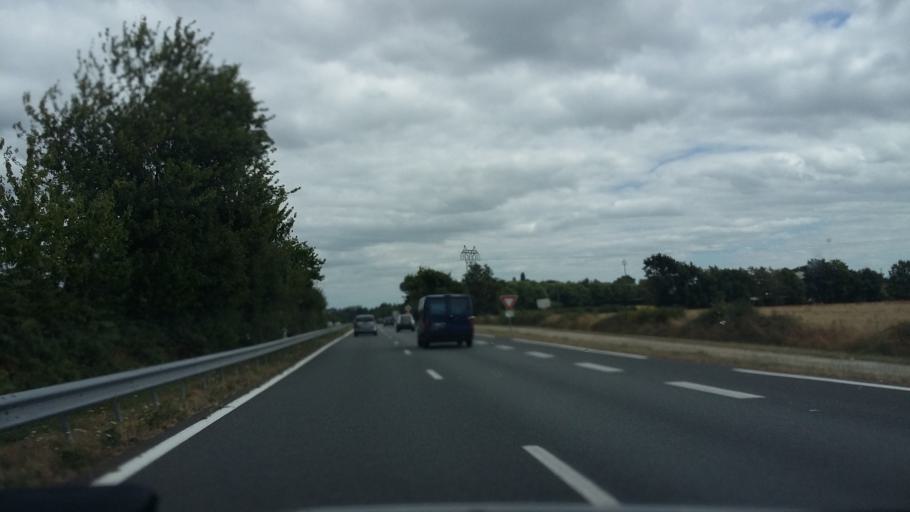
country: FR
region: Pays de la Loire
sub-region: Departement de la Vendee
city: Mouilleron-le-Captif
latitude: 46.6909
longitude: -1.4682
